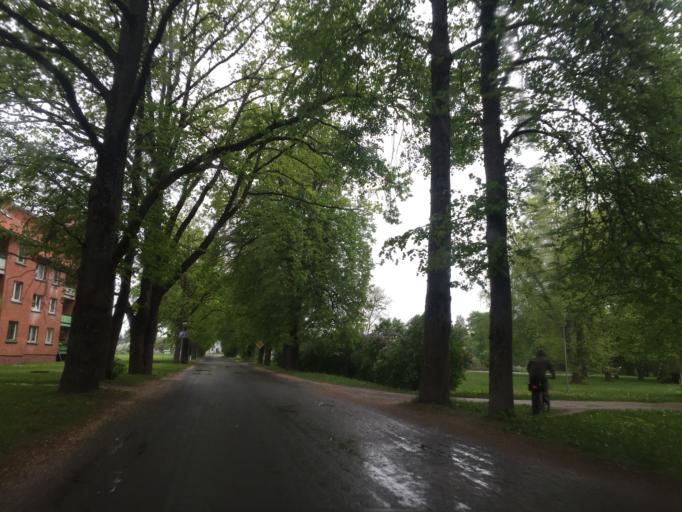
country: LV
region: Lielvarde
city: Lielvarde
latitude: 56.7133
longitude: 24.8330
